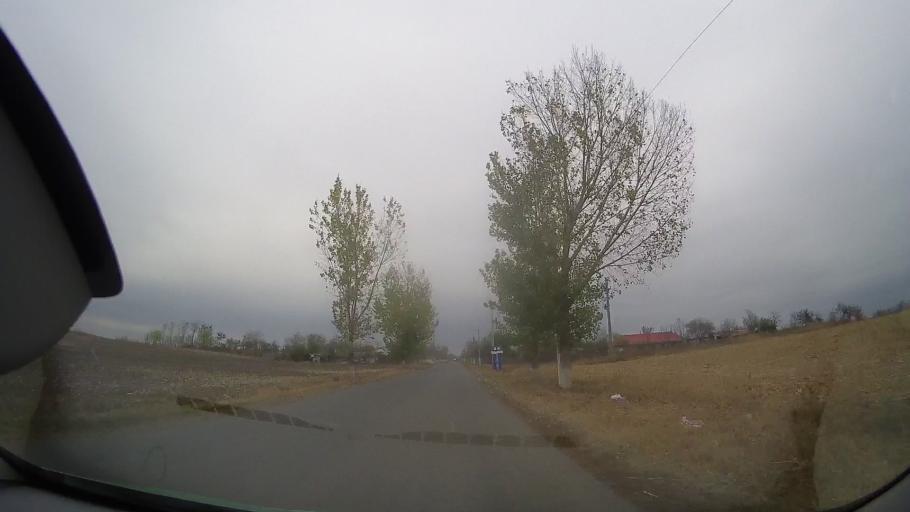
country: RO
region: Braila
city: Dudesti
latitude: 44.8731
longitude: 27.4296
